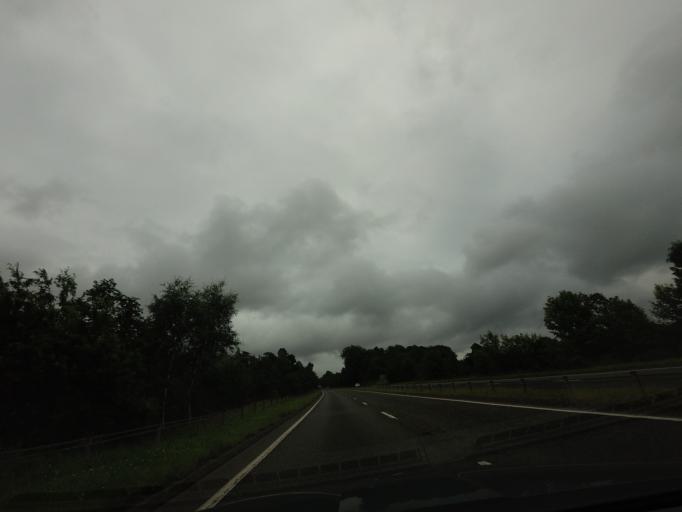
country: GB
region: Scotland
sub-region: Highland
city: Inverness
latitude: 57.4677
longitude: -4.1792
